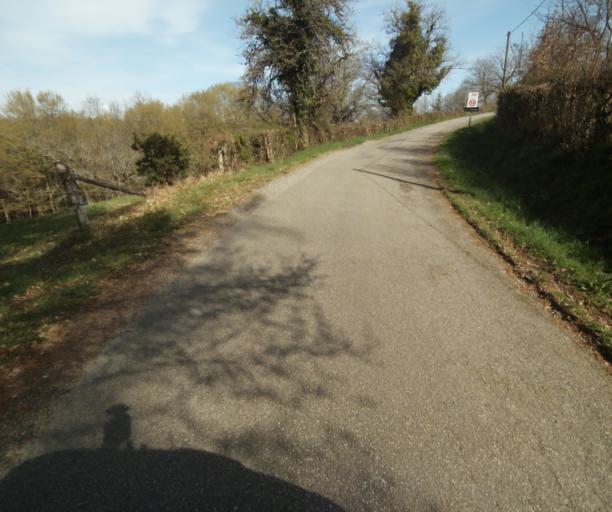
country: FR
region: Limousin
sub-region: Departement de la Correze
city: Naves
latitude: 45.3536
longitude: 1.7596
